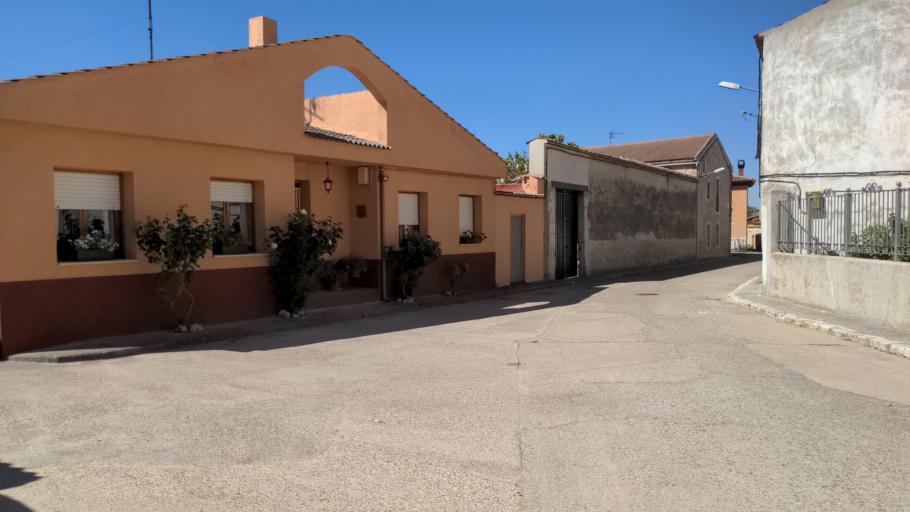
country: ES
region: Castille and Leon
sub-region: Provincia de Valladolid
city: Tudela de Duero
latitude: 41.5376
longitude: -4.5336
